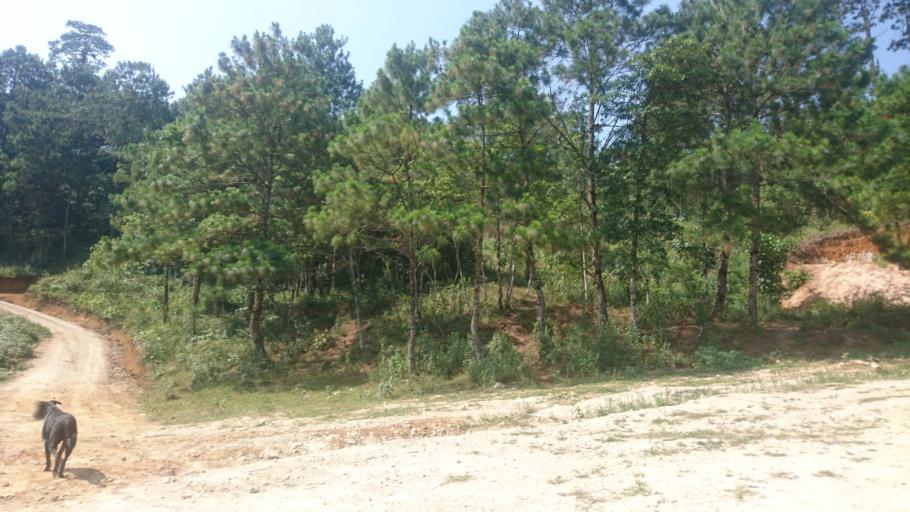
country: GT
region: Huehuetenango
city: Union
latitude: 16.0731
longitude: -91.6824
